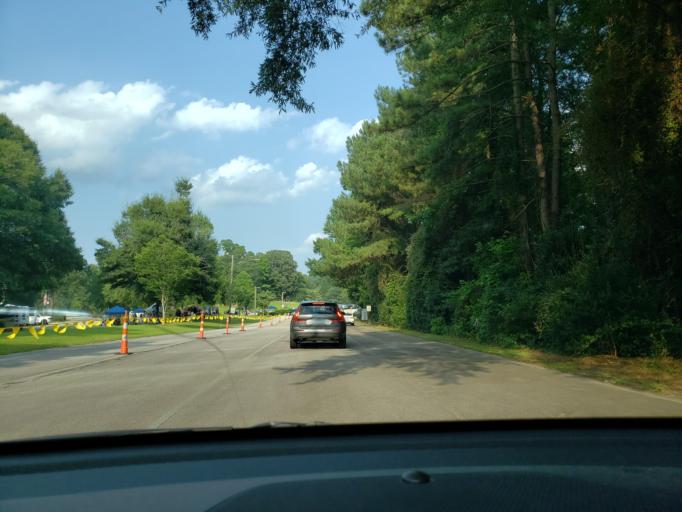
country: US
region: North Carolina
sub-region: Wake County
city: Garner
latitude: 35.7533
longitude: -78.5817
